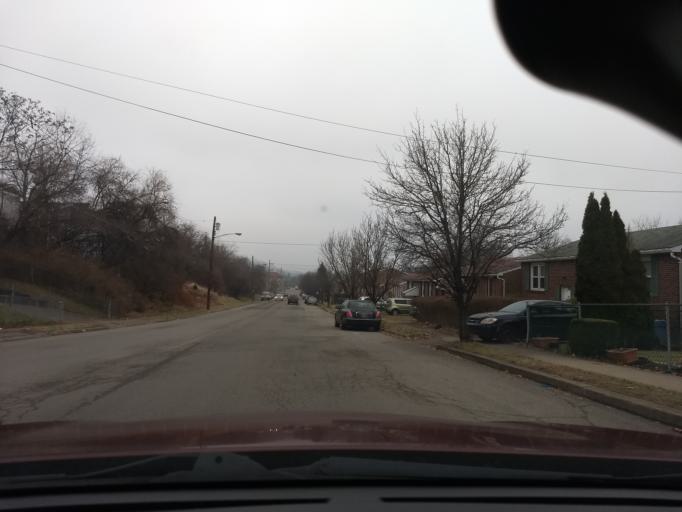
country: US
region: Pennsylvania
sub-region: Allegheny County
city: Rankin
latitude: 40.4119
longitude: -79.8810
